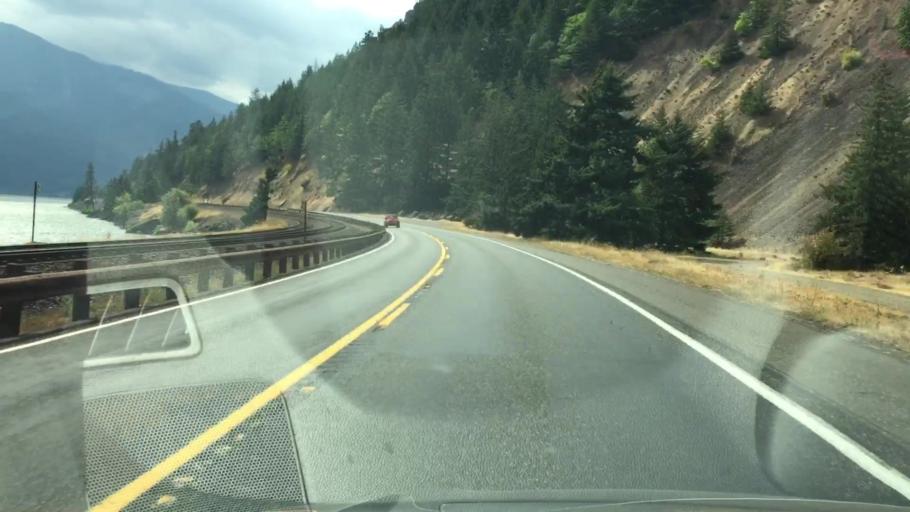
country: US
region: Washington
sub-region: Skamania County
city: Carson
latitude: 45.7101
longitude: -121.6750
